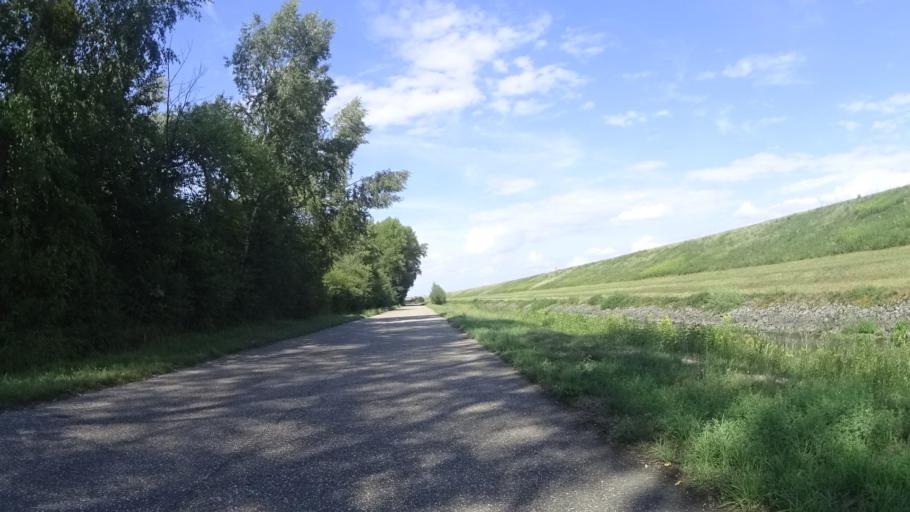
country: DE
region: Baden-Wuerttemberg
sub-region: Karlsruhe Region
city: Hugelsheim
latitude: 48.8080
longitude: 8.0905
